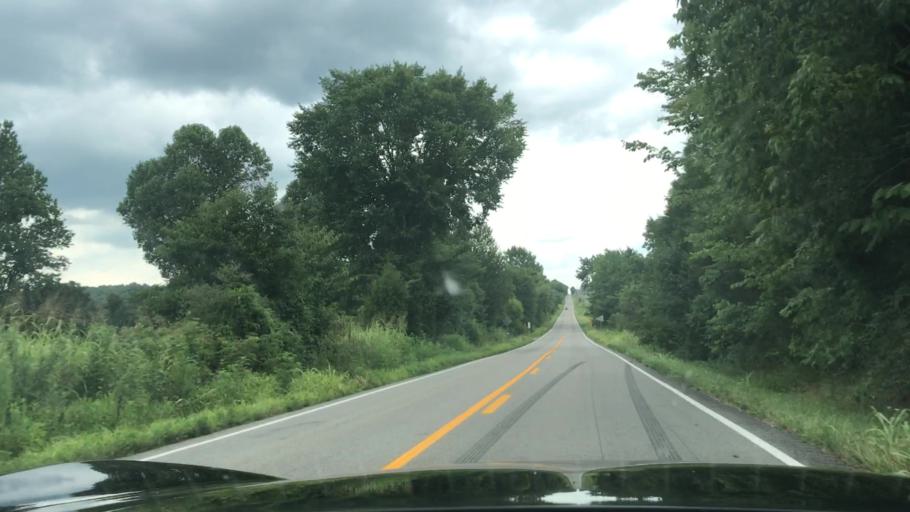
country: US
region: Kentucky
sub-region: Muhlenberg County
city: Central City
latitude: 37.1957
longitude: -86.9867
